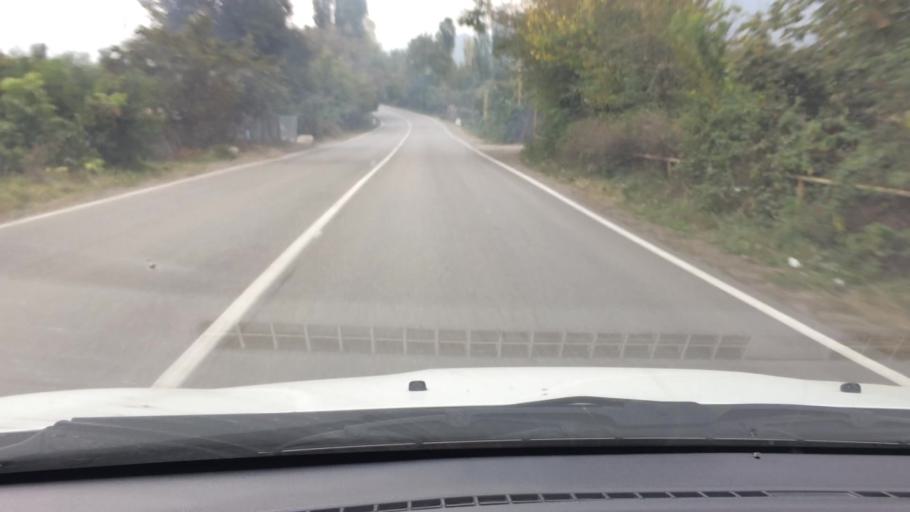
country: AM
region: Tavush
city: Bagratashen
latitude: 41.2348
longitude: 44.8098
